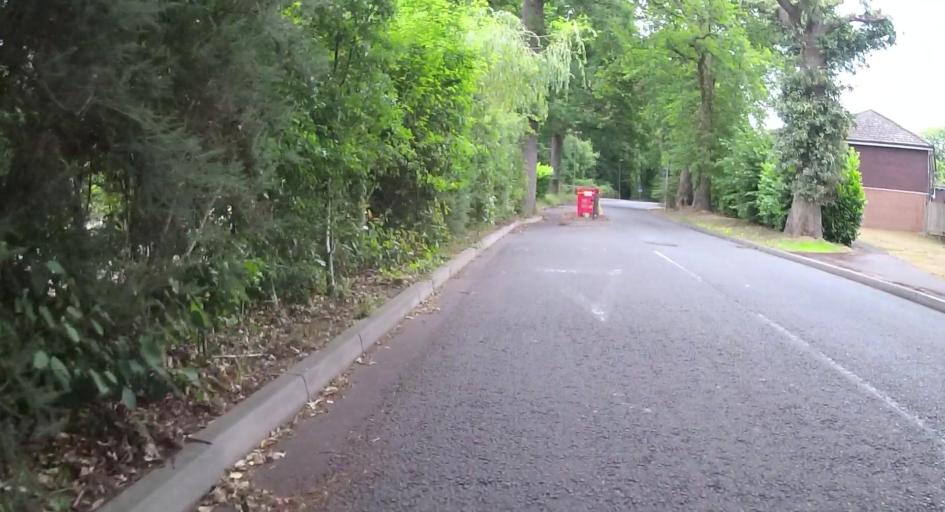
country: GB
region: England
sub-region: Hampshire
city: Fleet
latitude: 51.2540
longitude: -0.8279
